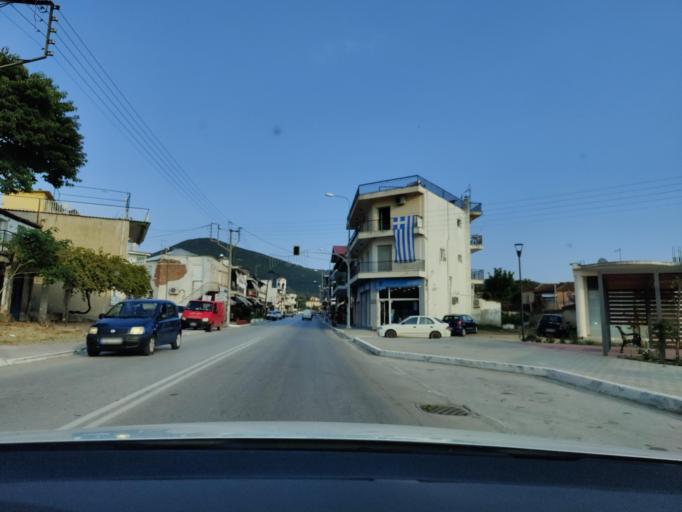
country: GR
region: East Macedonia and Thrace
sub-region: Nomos Kavalas
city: Amygdaleonas
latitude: 40.9643
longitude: 24.3574
